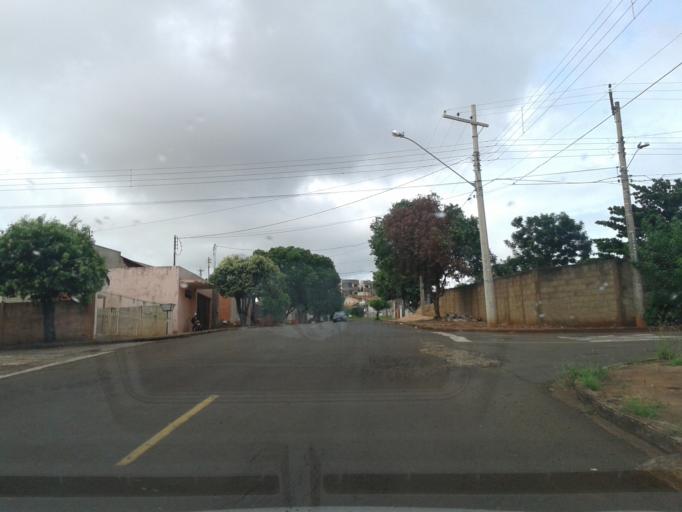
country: BR
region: Minas Gerais
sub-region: Ituiutaba
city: Ituiutaba
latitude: -18.9642
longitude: -49.4616
